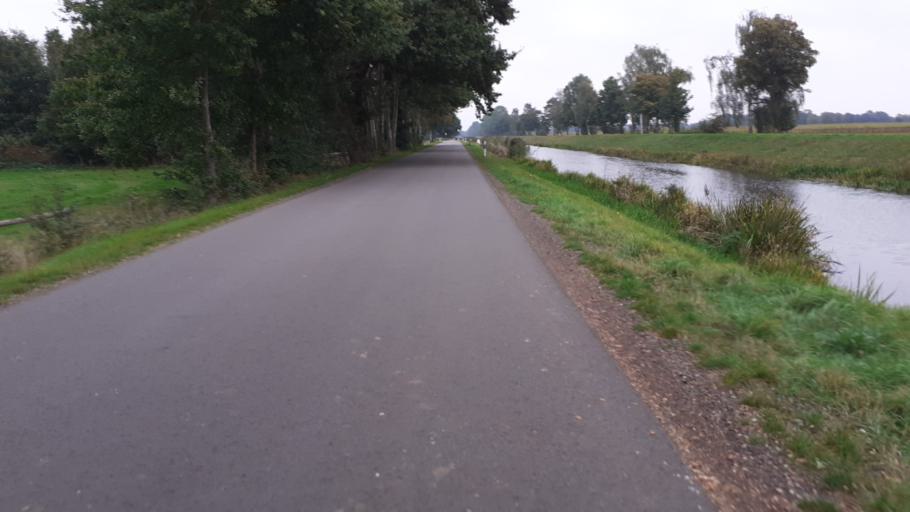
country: DE
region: Lower Saxony
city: Oldenburg
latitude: 53.1147
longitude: 8.2987
